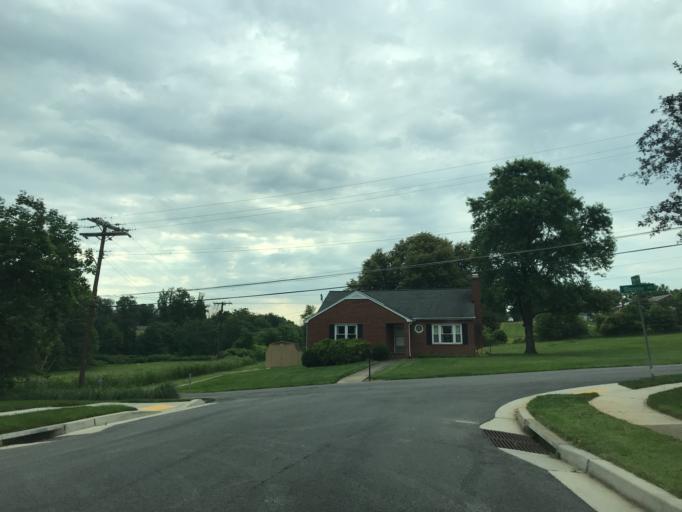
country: US
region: Maryland
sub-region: Baltimore County
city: Overlea
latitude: 39.3633
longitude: -76.5118
